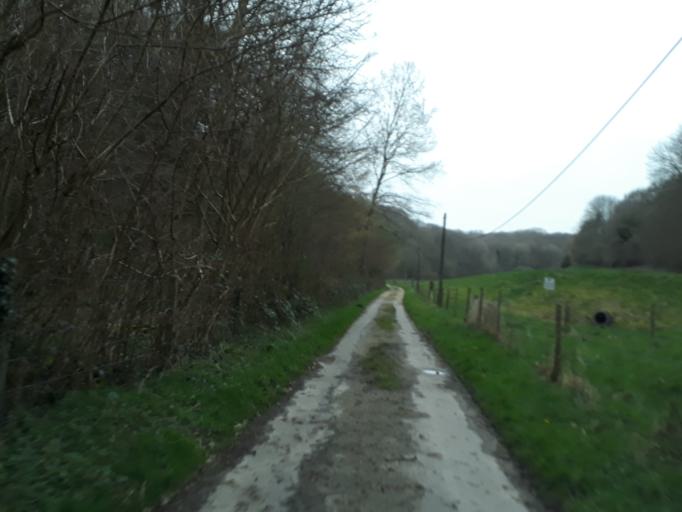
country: FR
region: Haute-Normandie
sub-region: Departement de la Seine-Maritime
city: Yport
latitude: 49.7278
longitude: 0.2961
